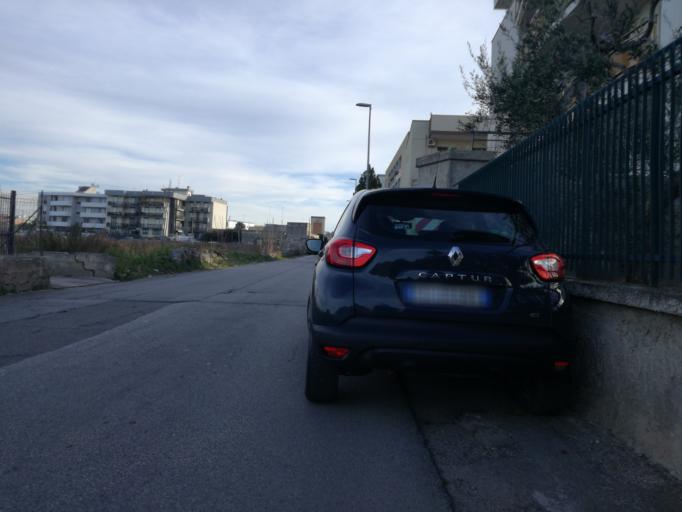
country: IT
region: Apulia
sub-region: Provincia di Bari
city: Capurso
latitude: 41.0518
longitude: 16.9217
